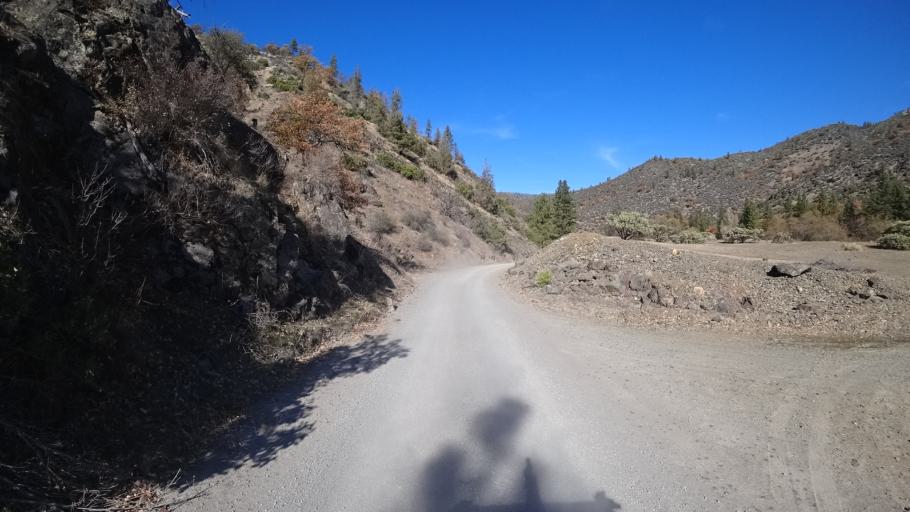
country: US
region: California
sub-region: Siskiyou County
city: Yreka
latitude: 41.8428
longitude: -122.6845
